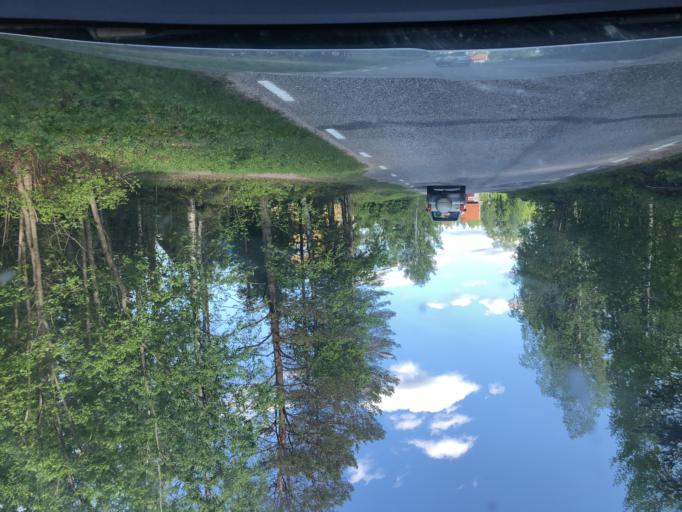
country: SE
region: Norrbotten
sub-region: Kalix Kommun
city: Kalix
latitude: 66.0582
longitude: 23.1950
